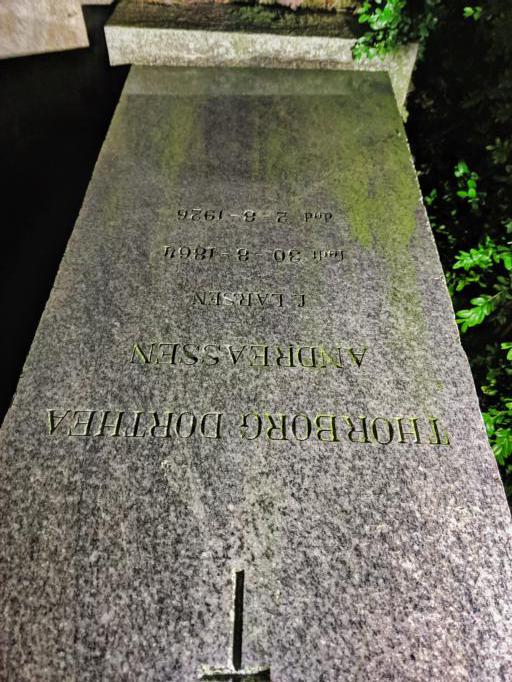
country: NO
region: Rogaland
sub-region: Hjelmeland
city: Hjelmelandsvagen
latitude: 59.1559
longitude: 6.1909
